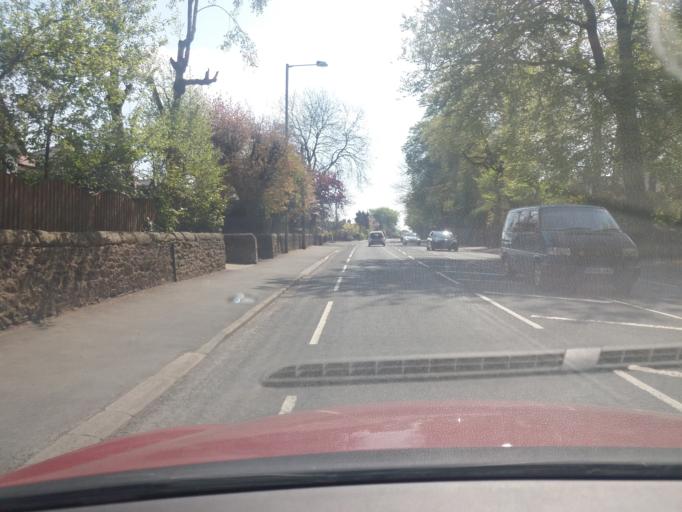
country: GB
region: England
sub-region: Lancashire
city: Clayton-le-Woods
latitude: 53.6828
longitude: -2.6382
